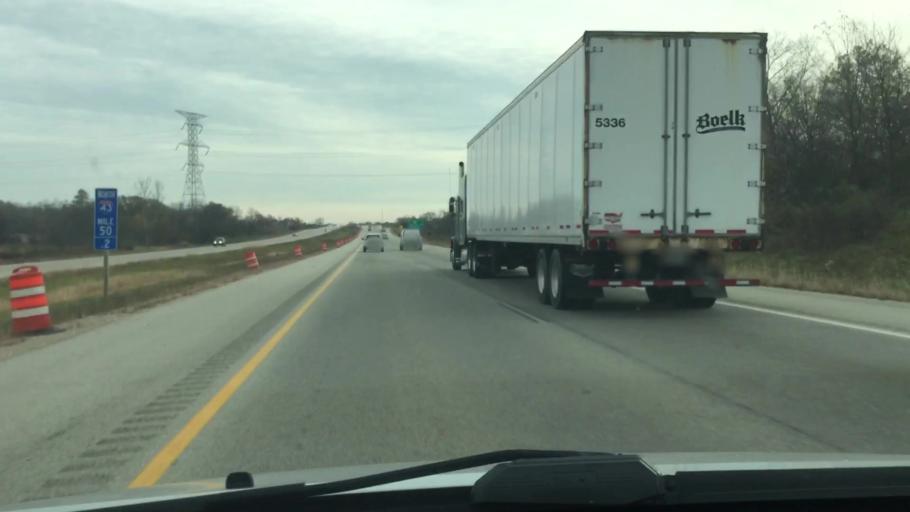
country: US
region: Wisconsin
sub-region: Waukesha County
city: Big Bend
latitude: 42.9082
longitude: -88.2265
